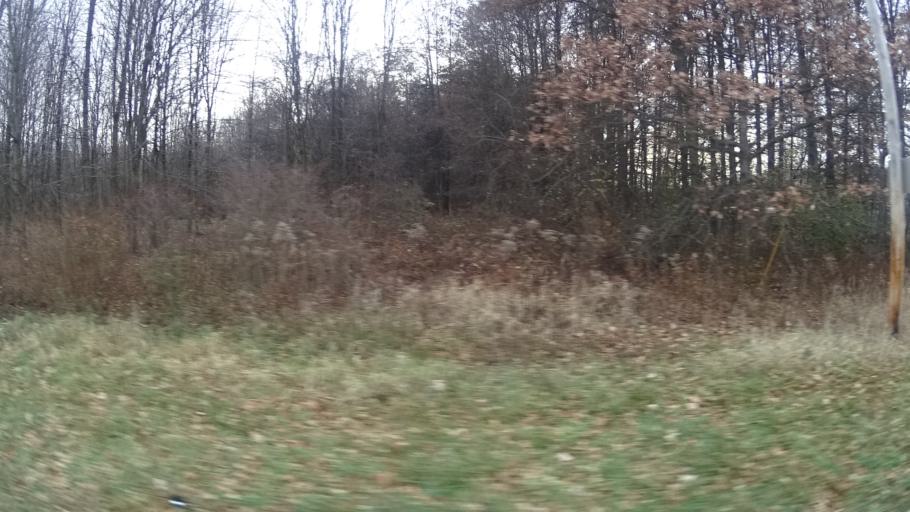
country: US
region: Ohio
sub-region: Lorain County
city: Eaton Estates
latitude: 41.3512
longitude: -81.9710
